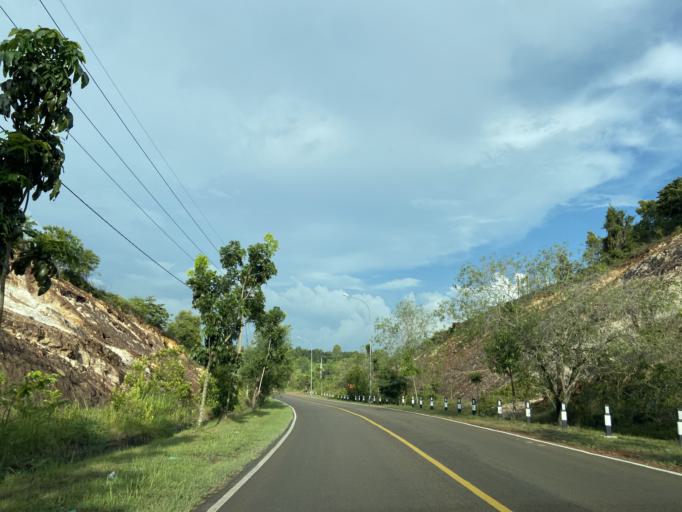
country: ID
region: Riau Islands
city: Tanjungpinang
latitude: 0.9506
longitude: 104.0685
